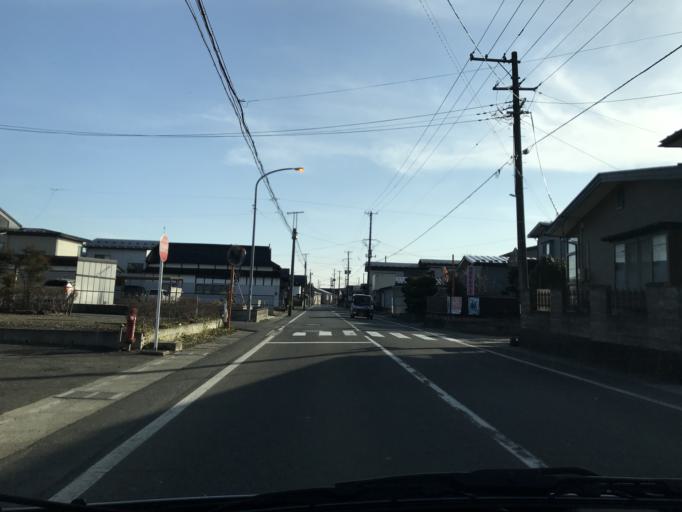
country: JP
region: Iwate
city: Kitakami
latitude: 39.2606
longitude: 141.1140
